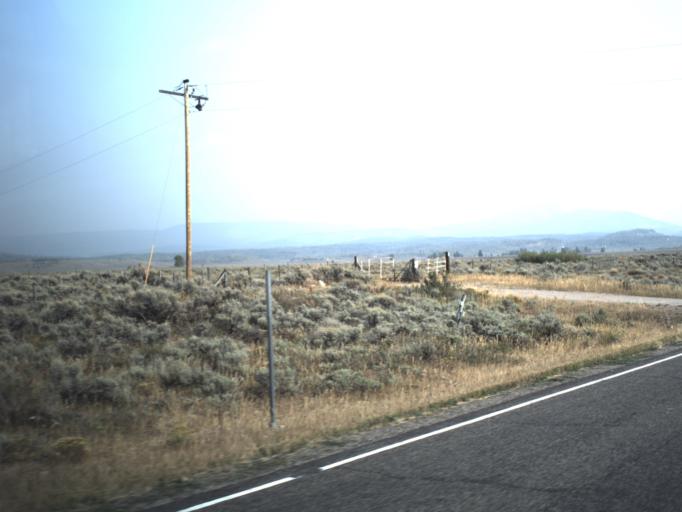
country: US
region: Wyoming
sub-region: Uinta County
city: Evanston
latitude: 40.9605
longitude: -110.8448
